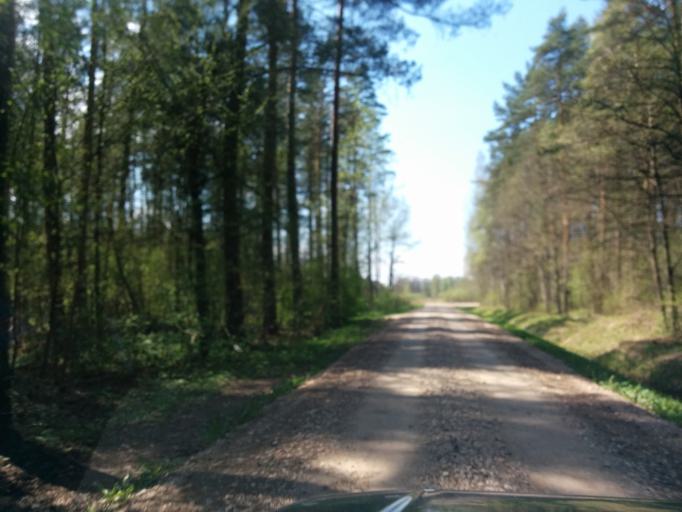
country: LV
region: Jelgava
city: Jelgava
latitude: 56.6202
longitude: 23.7410
